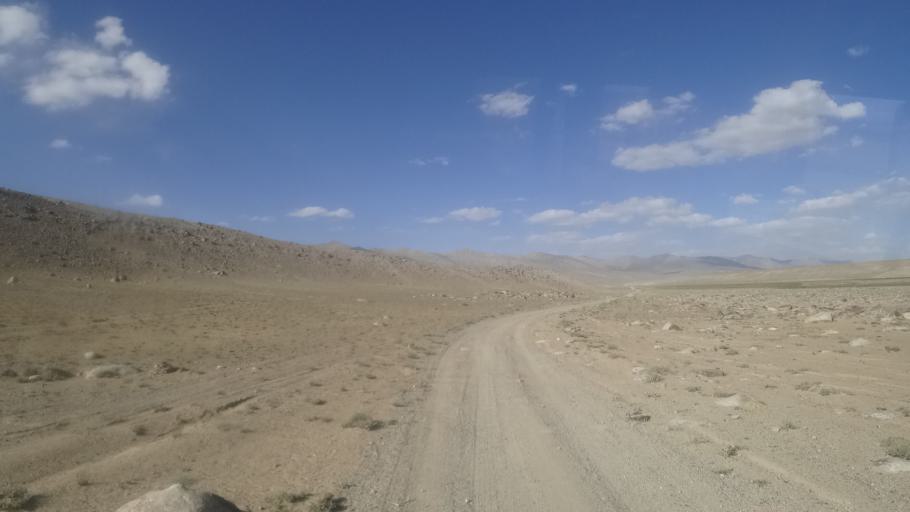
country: AF
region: Badakhshan
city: Khandud
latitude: 37.4260
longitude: 73.2392
